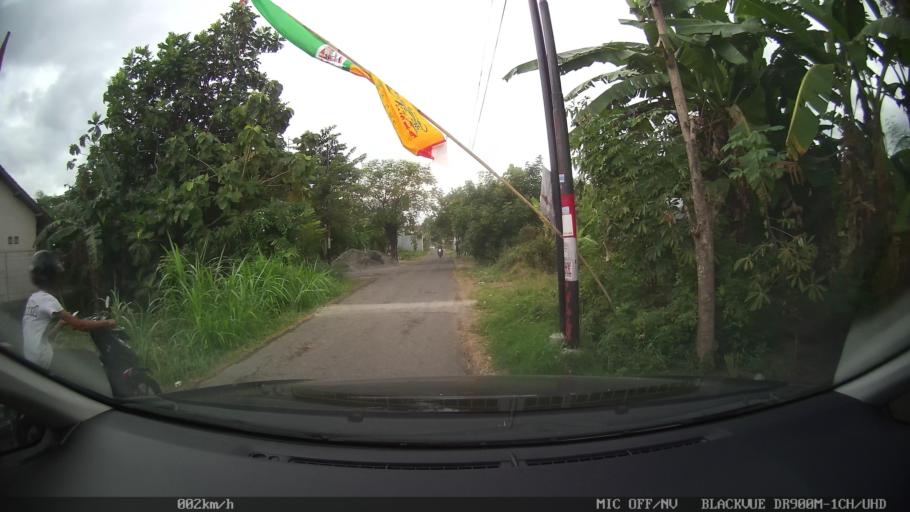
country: ID
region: Daerah Istimewa Yogyakarta
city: Sewon
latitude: -7.8330
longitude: 110.4094
